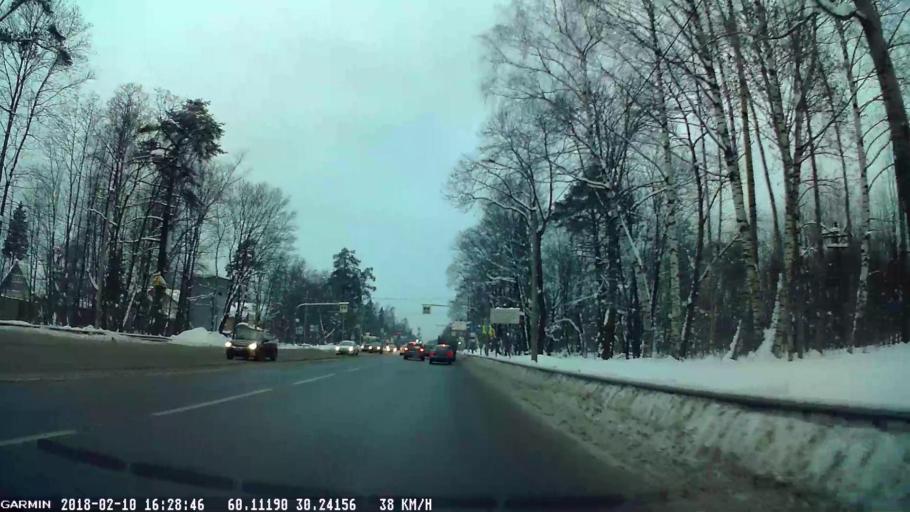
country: RU
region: St.-Petersburg
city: Levashovo
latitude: 60.1120
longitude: 30.2415
